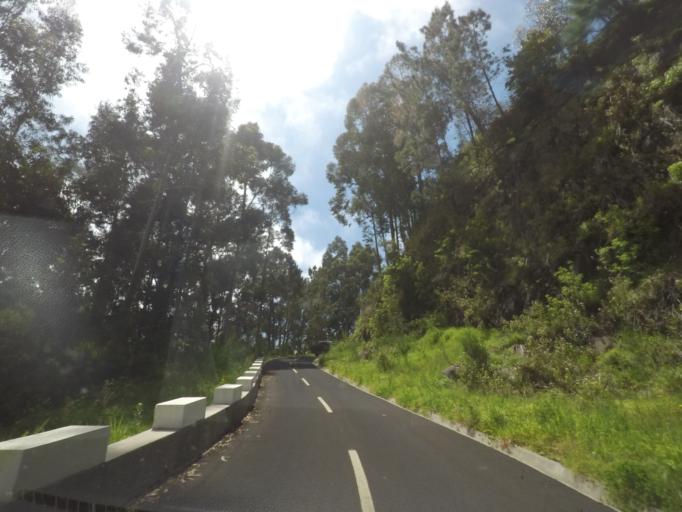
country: PT
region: Madeira
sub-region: Calheta
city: Arco da Calheta
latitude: 32.7289
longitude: -17.1203
